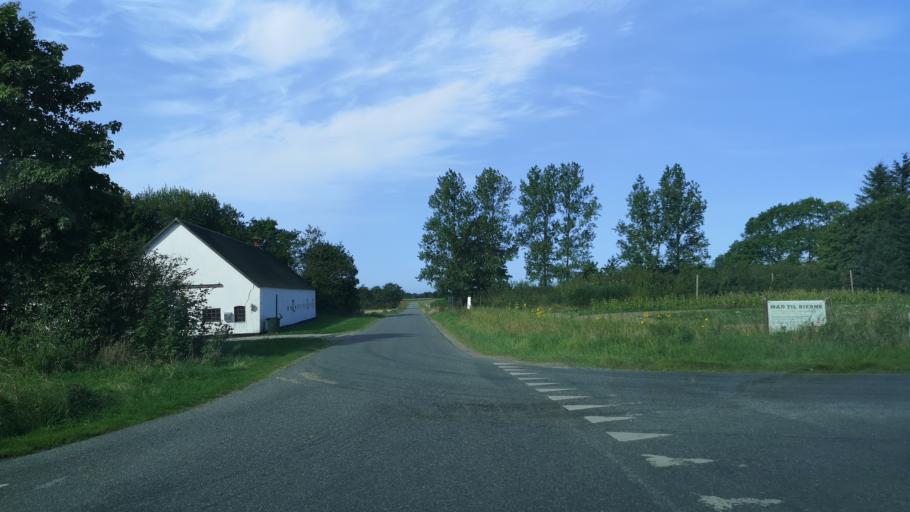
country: DK
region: Central Jutland
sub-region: Herning Kommune
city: Hammerum
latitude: 56.1568
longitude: 9.1030
